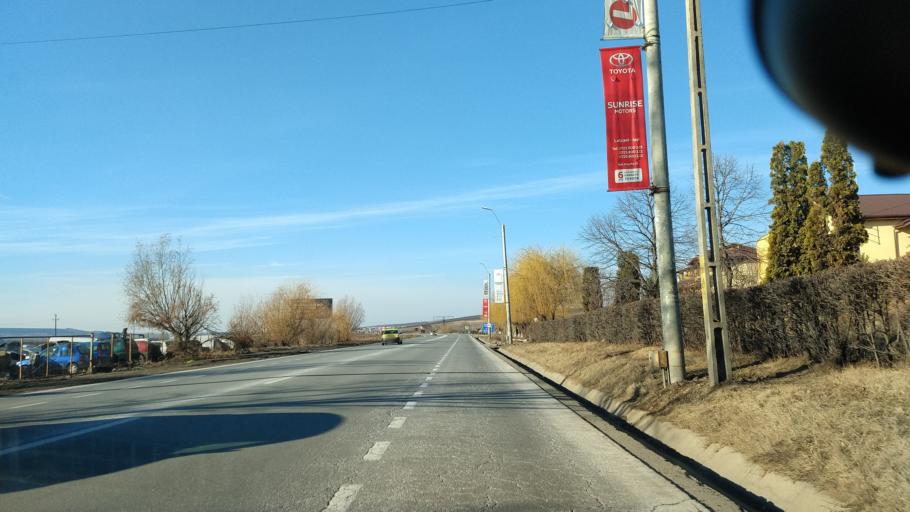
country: RO
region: Iasi
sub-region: Comuna Letcani
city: Cogeasca
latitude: 47.2020
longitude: 27.3844
